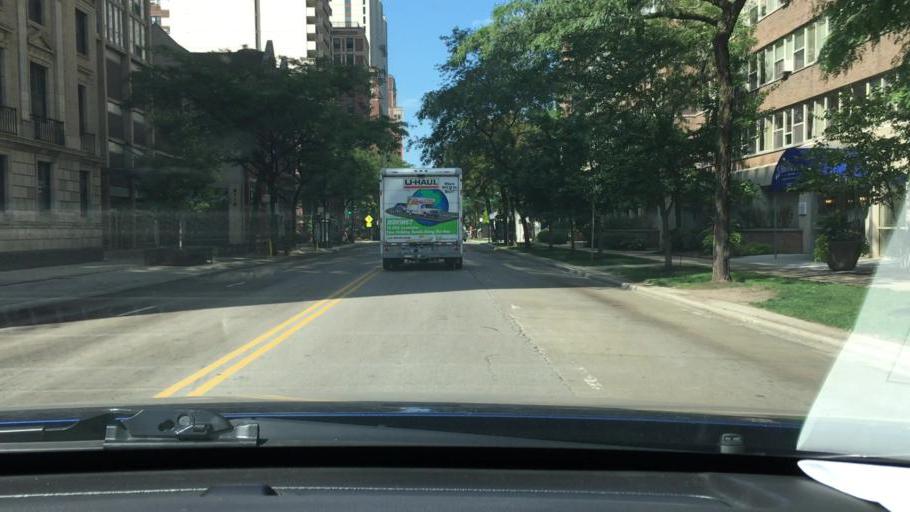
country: US
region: Illinois
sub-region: Cook County
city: Chicago
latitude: 41.9377
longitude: -87.6394
